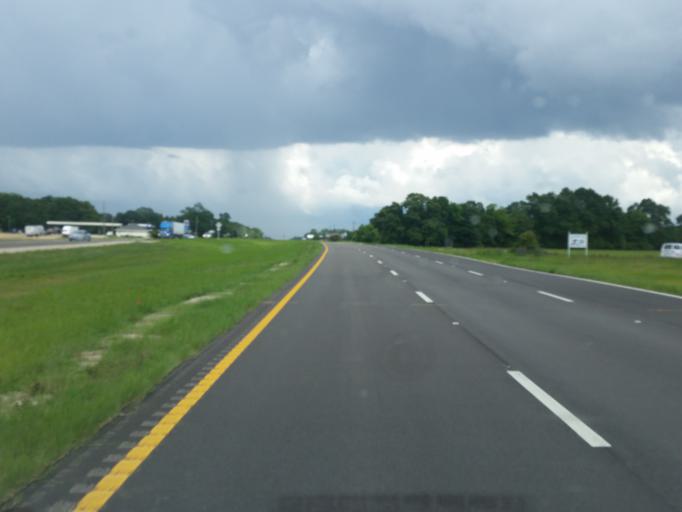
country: US
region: Mississippi
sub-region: George County
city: Lucedale
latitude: 30.9247
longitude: -88.5132
